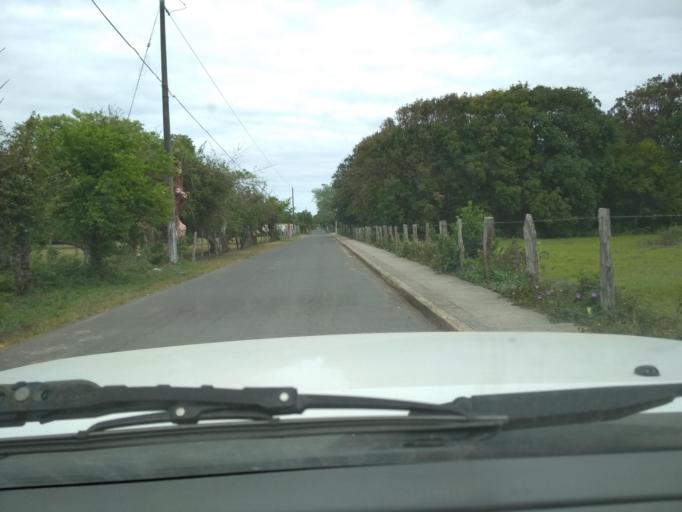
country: MX
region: Veracruz
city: El Tejar
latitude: 19.0737
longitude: -96.1458
